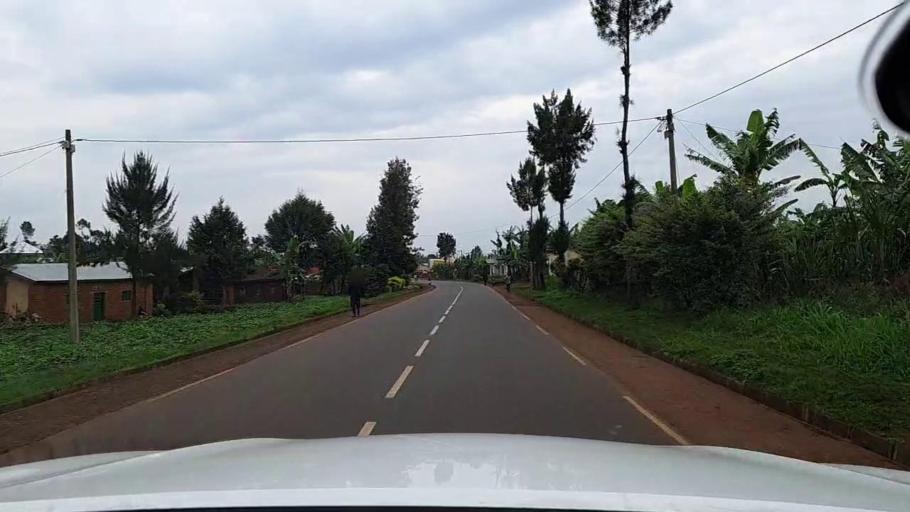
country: RW
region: Western Province
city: Cyangugu
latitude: -2.6027
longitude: 28.9331
